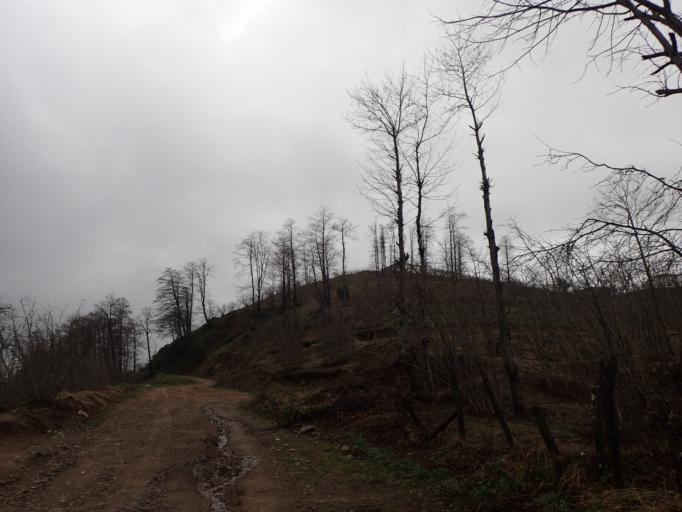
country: TR
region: Ordu
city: Camas
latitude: 40.8613
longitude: 37.5166
